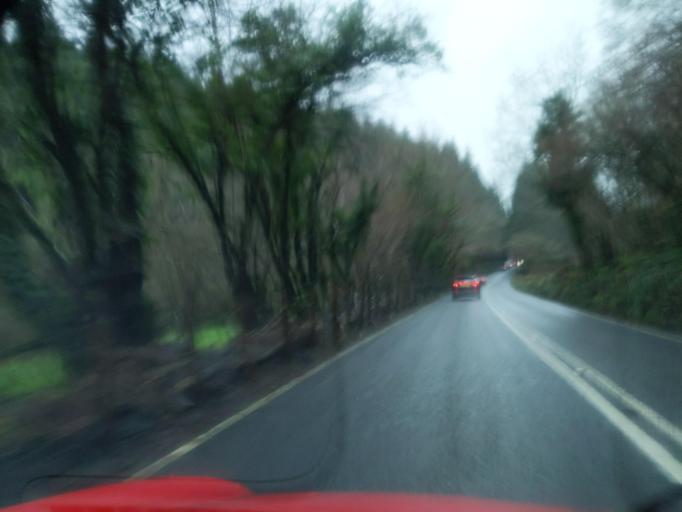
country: GB
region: England
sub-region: Cornwall
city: South Hill
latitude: 50.5626
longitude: -4.3332
